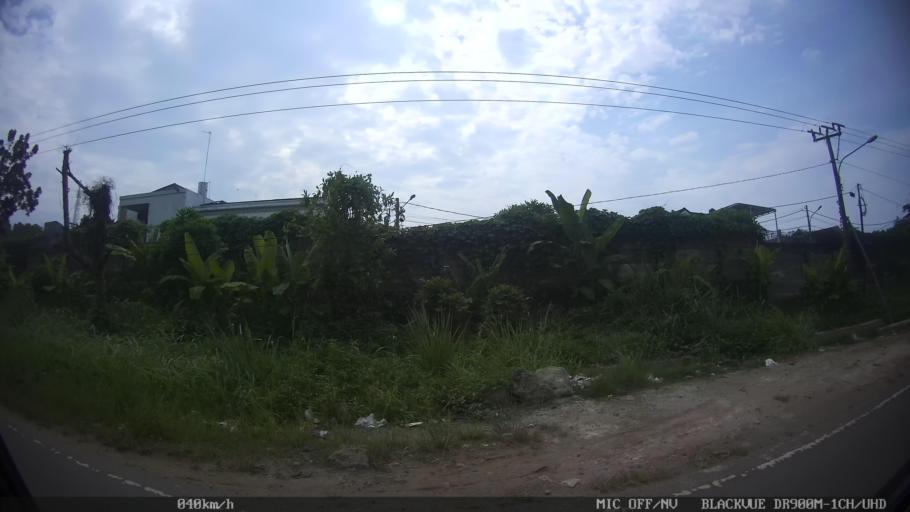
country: ID
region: Lampung
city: Bandarlampung
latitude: -5.4475
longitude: 105.2426
